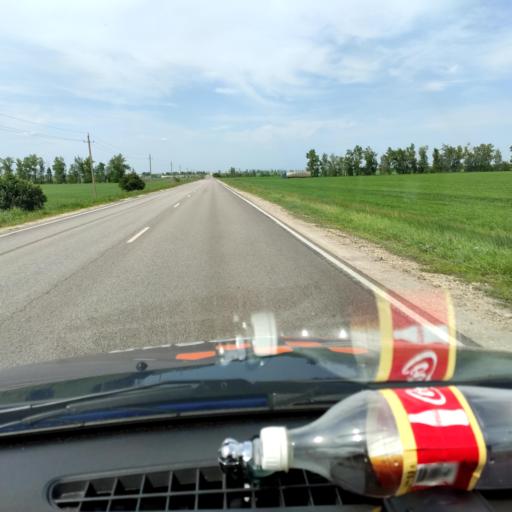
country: RU
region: Voronezj
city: Novaya Usman'
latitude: 51.5620
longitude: 39.3760
